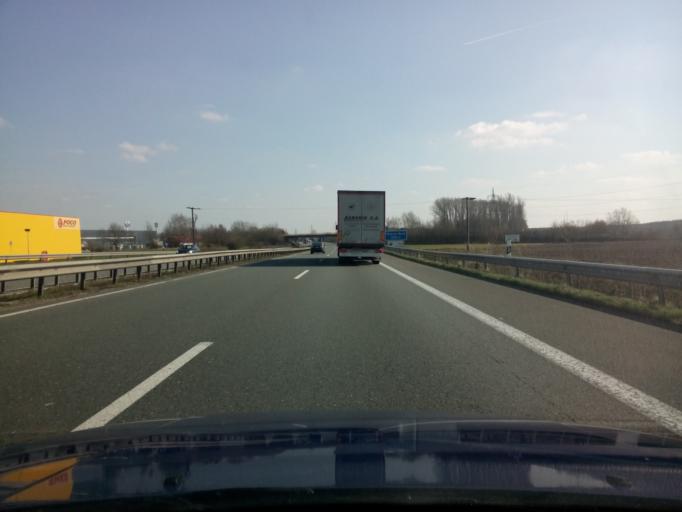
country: DE
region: North Rhine-Westphalia
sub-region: Regierungsbezirk Munster
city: Rheine
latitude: 52.3320
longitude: 7.4160
